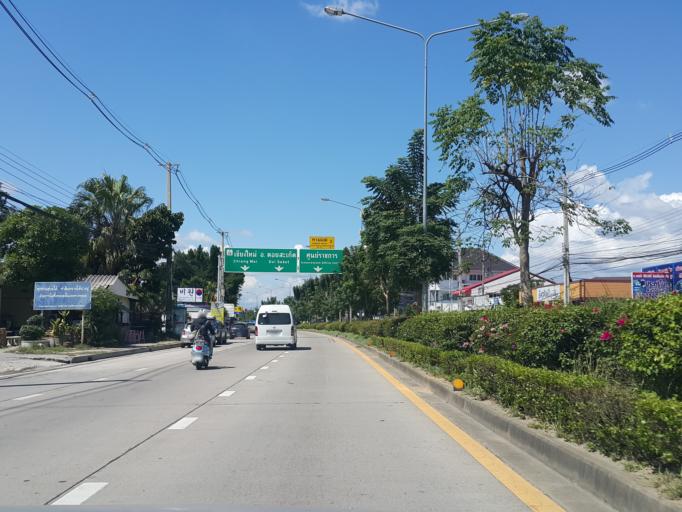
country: TH
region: Chiang Mai
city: San Sai
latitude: 18.8043
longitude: 99.0302
